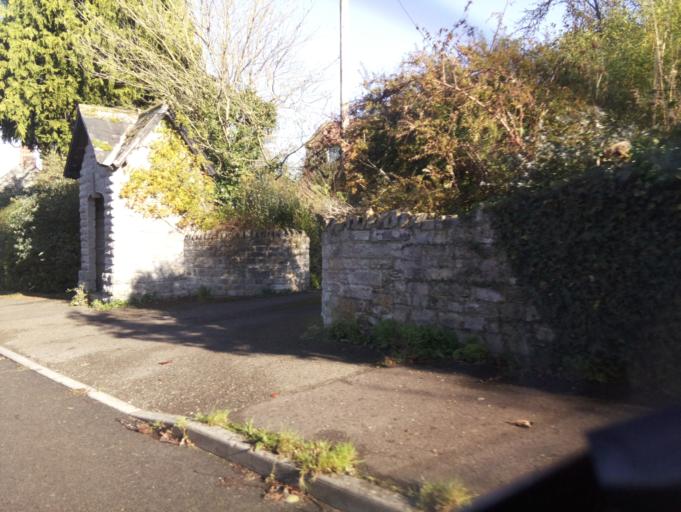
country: GB
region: England
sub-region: Somerset
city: Martock
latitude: 51.0238
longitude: -2.7590
